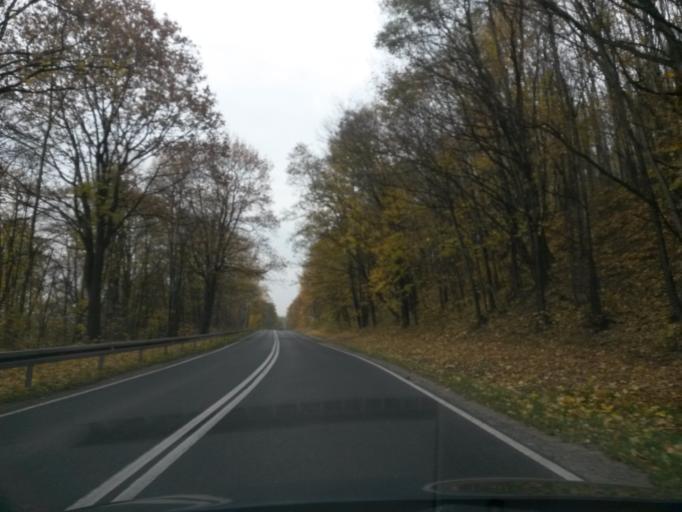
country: PL
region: Lower Silesian Voivodeship
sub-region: Powiat klodzki
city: Klodzko
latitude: 50.3820
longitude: 16.6686
